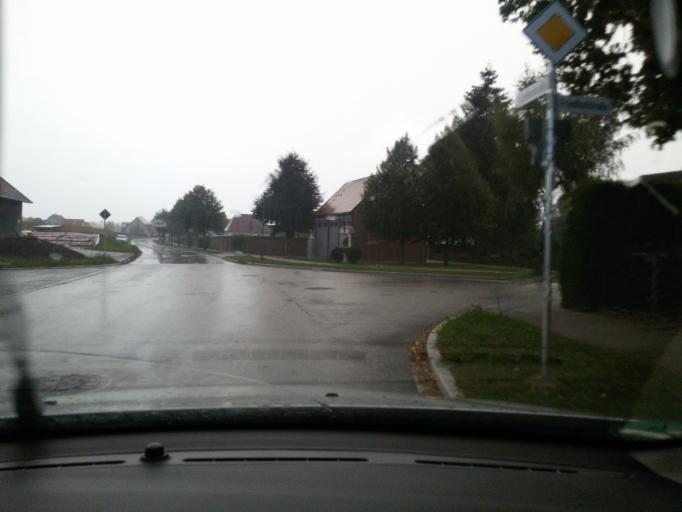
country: DE
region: Bavaria
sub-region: Swabia
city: Hiltenfingen
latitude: 48.1606
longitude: 10.7238
